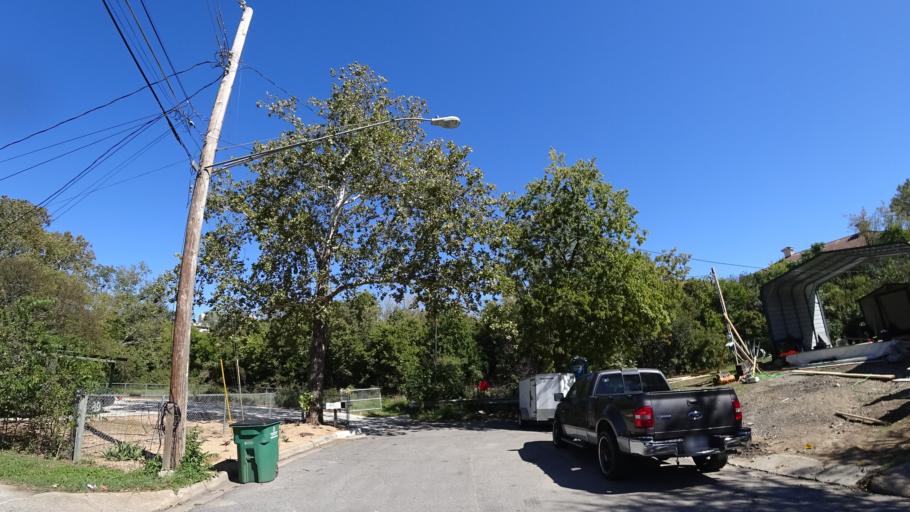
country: US
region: Texas
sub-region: Travis County
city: Rollingwood
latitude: 30.2243
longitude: -97.7772
